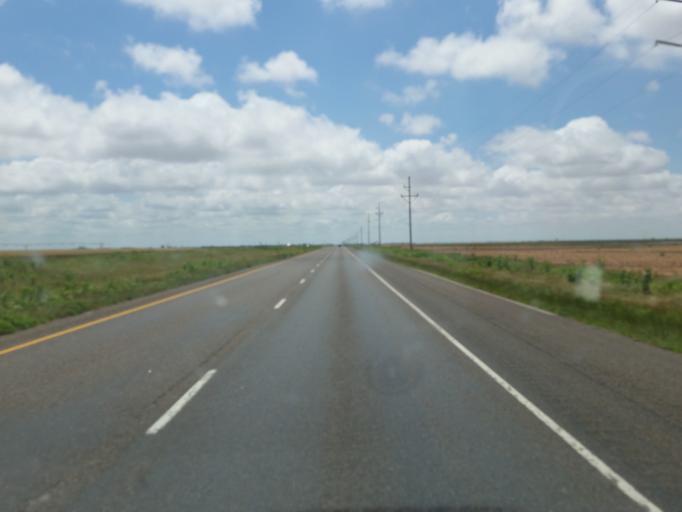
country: US
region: Texas
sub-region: Lubbock County
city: Slaton
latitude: 33.3911
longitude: -101.6002
